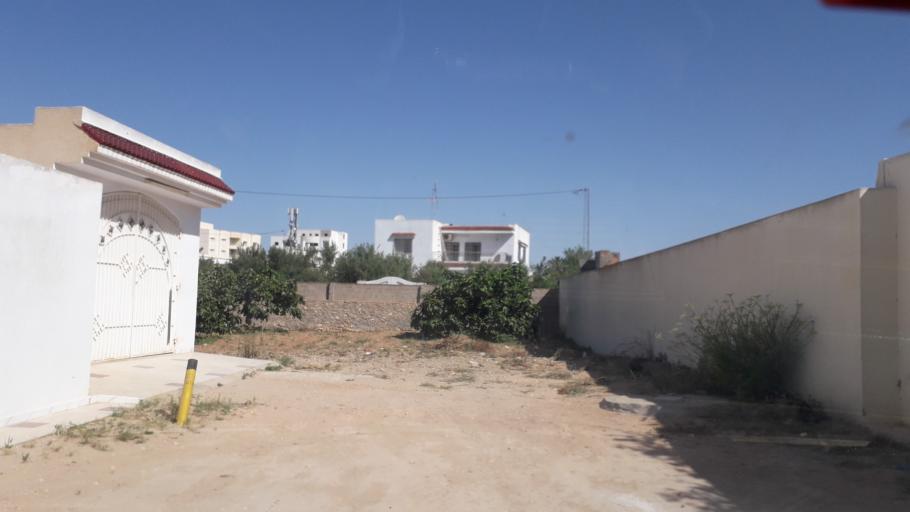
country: TN
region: Safaqis
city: Al Qarmadah
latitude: 34.8075
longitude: 10.7632
